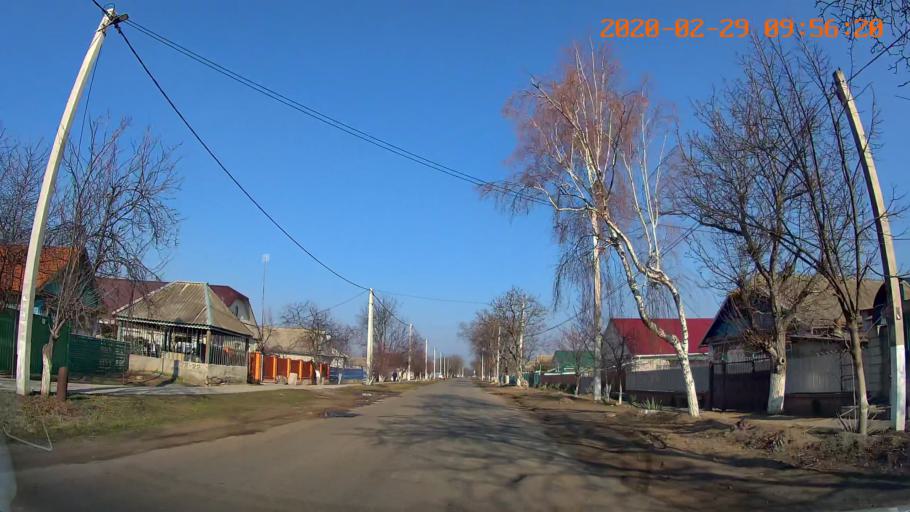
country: MD
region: Telenesti
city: Slobozia
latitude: 46.7415
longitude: 29.7053
